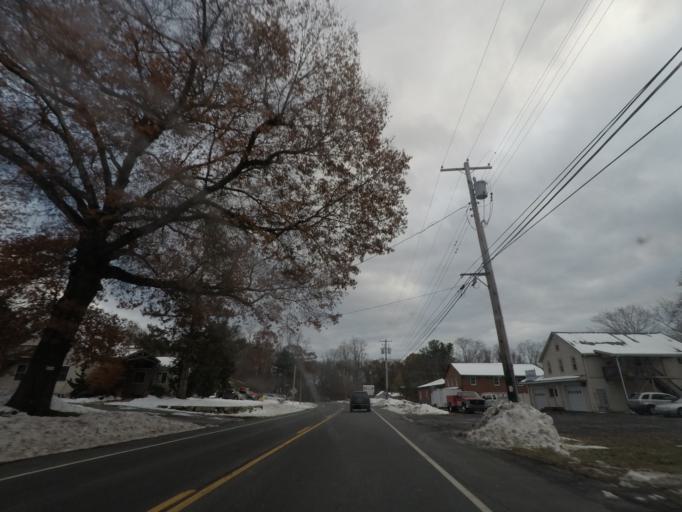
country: US
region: New York
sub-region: Ulster County
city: Tillson
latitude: 41.8285
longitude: -74.0692
